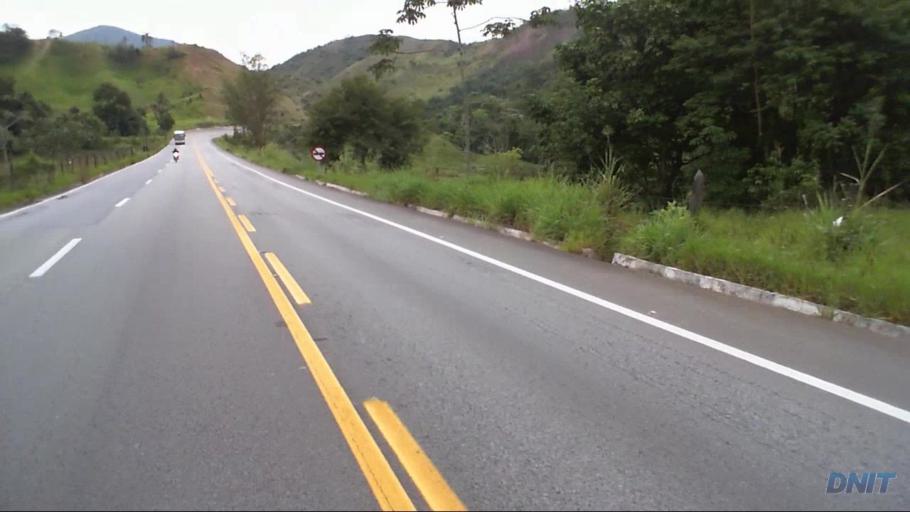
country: BR
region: Minas Gerais
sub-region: Timoteo
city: Timoteo
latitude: -19.6254
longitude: -42.8607
